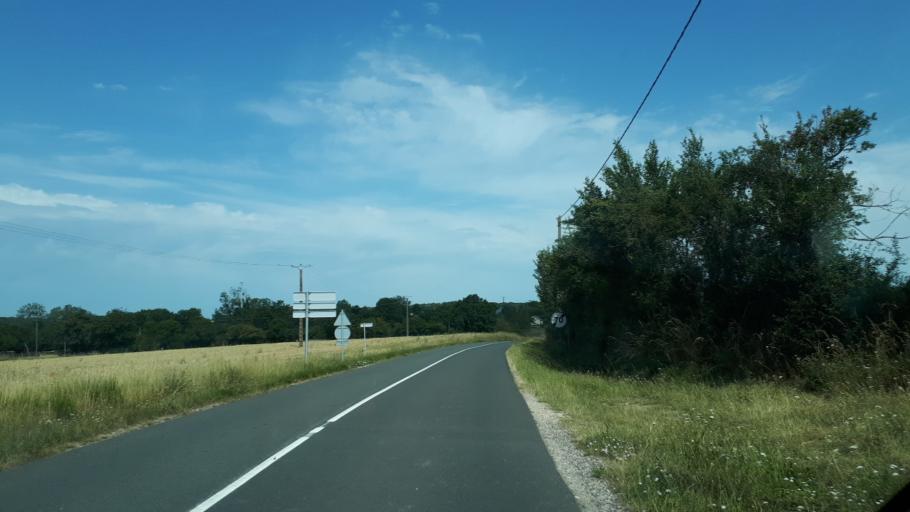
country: FR
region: Centre
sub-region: Departement du Loir-et-Cher
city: Droue
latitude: 47.9868
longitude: 1.0368
